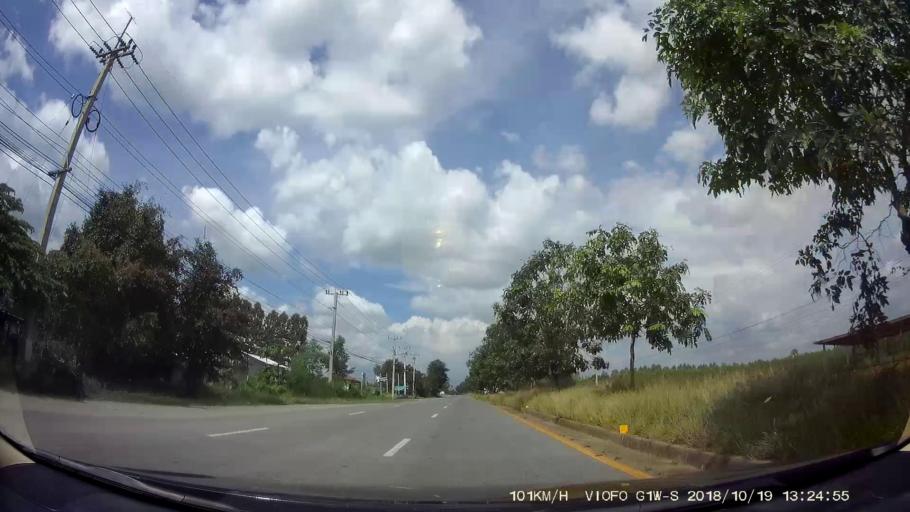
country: TH
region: Chaiyaphum
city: Chatturat
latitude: 15.5140
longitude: 101.8240
